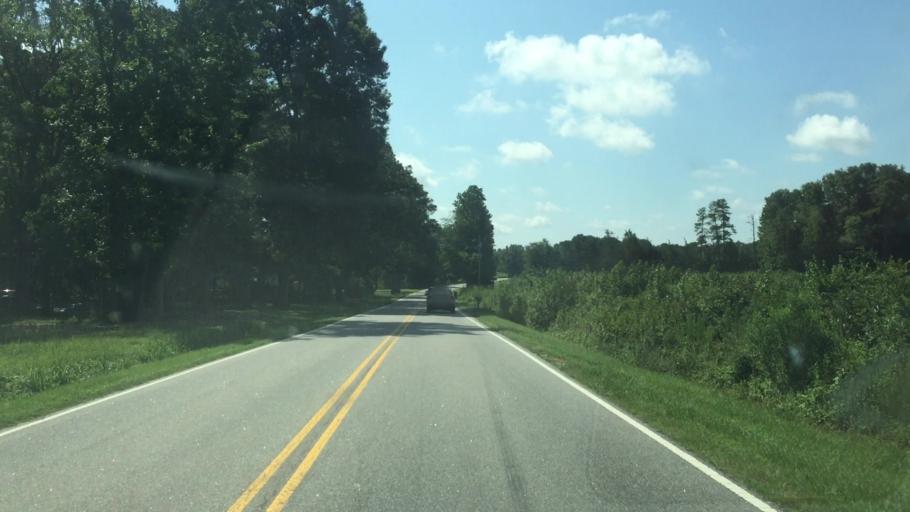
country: US
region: North Carolina
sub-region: Anson County
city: Burnsville
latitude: 35.0502
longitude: -80.2684
